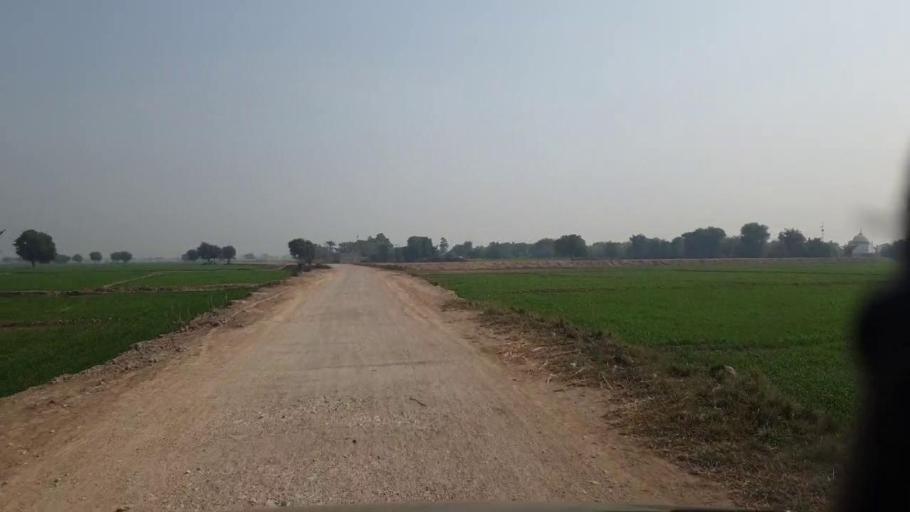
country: PK
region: Sindh
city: Shahdadpur
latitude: 26.0109
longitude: 68.5249
